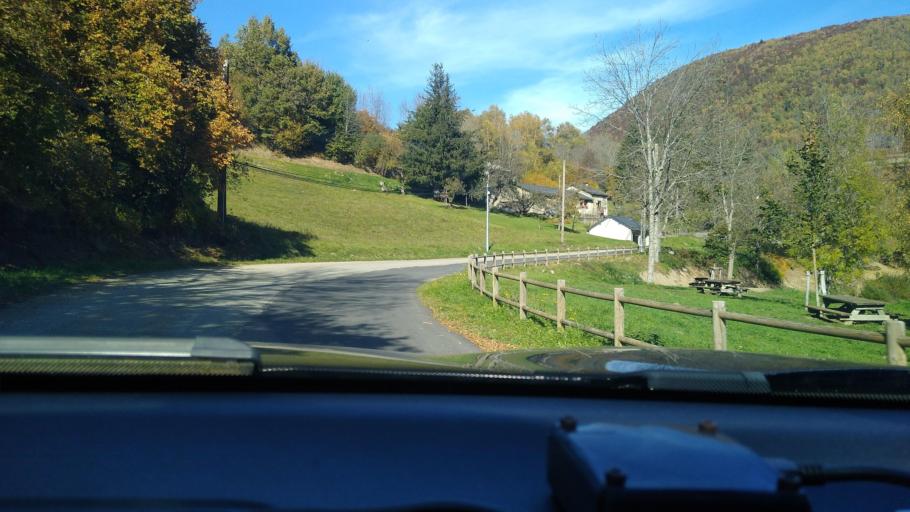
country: FR
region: Midi-Pyrenees
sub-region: Departement de l'Ariege
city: Ax-les-Thermes
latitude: 42.7234
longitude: 1.8849
